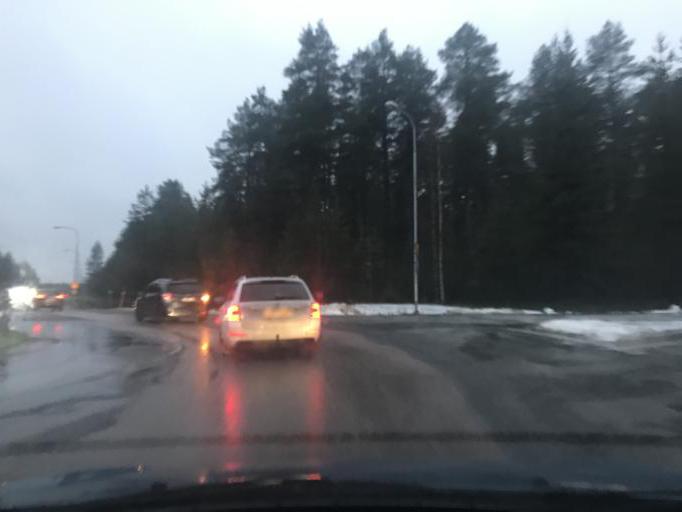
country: SE
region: Norrbotten
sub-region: Lulea Kommun
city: Gammelstad
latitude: 65.6254
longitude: 22.0361
